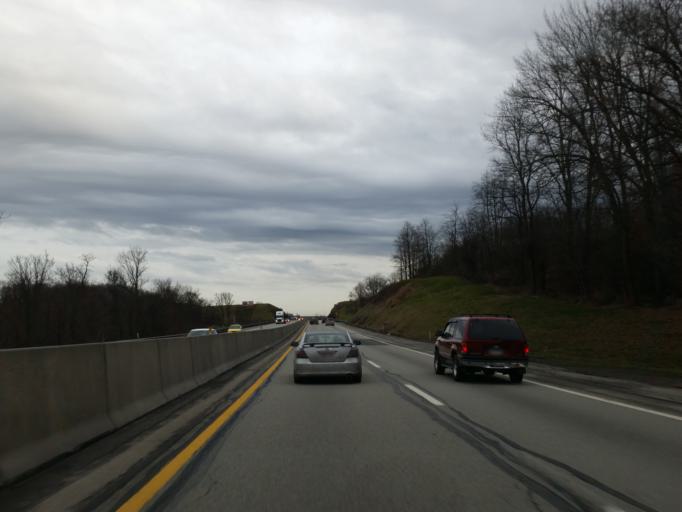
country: US
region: Pennsylvania
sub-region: Somerset County
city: Somerset
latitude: 40.0509
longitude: -79.1250
